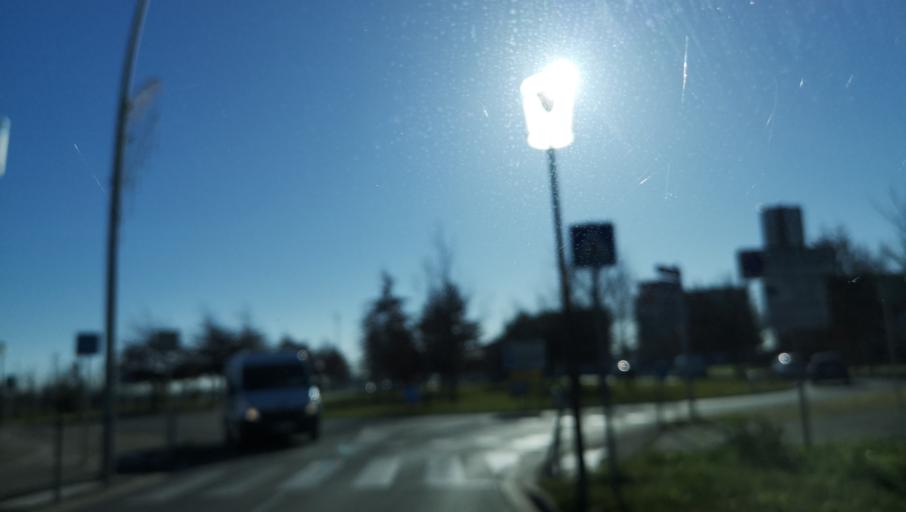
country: FR
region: Midi-Pyrenees
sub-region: Departement de la Haute-Garonne
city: Beauzelle
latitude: 43.6566
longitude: 1.3772
